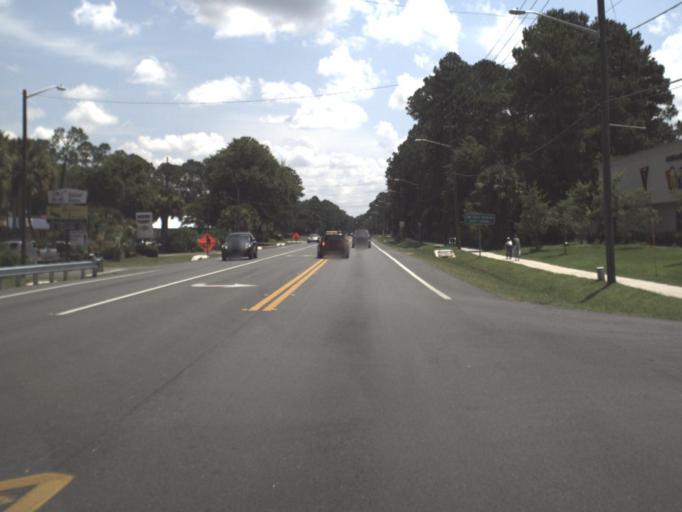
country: US
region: Florida
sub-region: Alachua County
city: Gainesville
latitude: 29.7017
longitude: -82.3674
